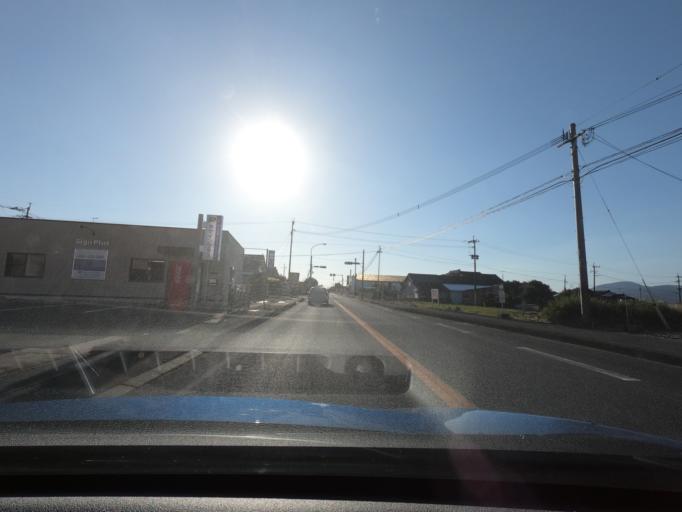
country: JP
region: Kagoshima
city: Izumi
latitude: 32.0974
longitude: 130.3029
